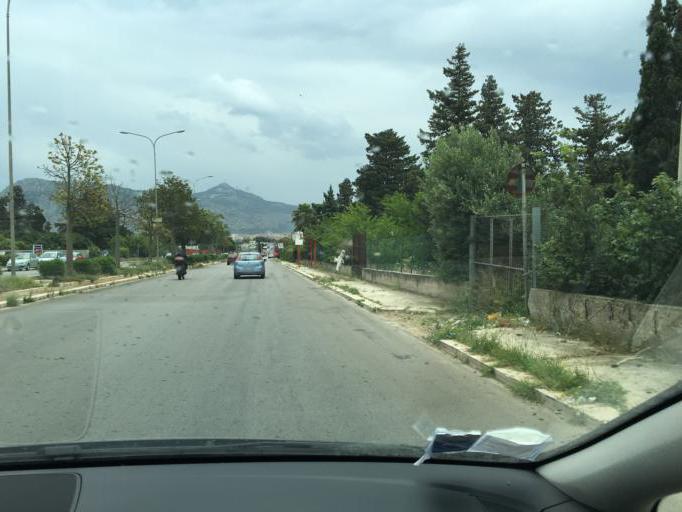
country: IT
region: Sicily
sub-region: Palermo
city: Isola delle Femmine
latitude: 38.1909
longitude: 13.2912
